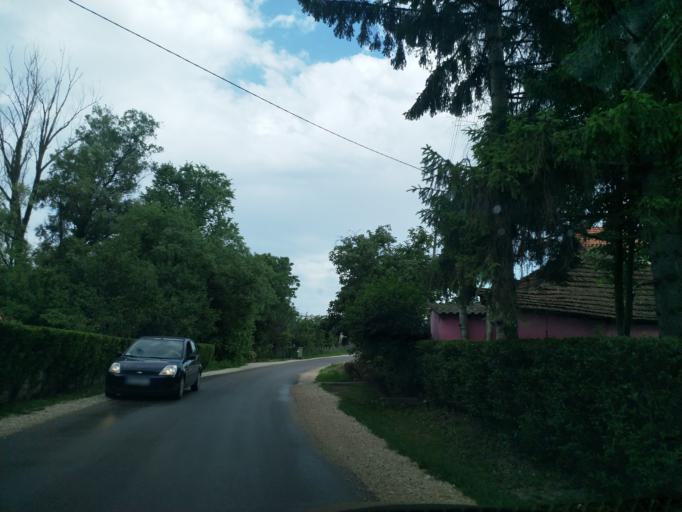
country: RS
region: Central Serbia
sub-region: Borski Okrug
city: Bor
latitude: 44.0127
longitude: 21.9843
